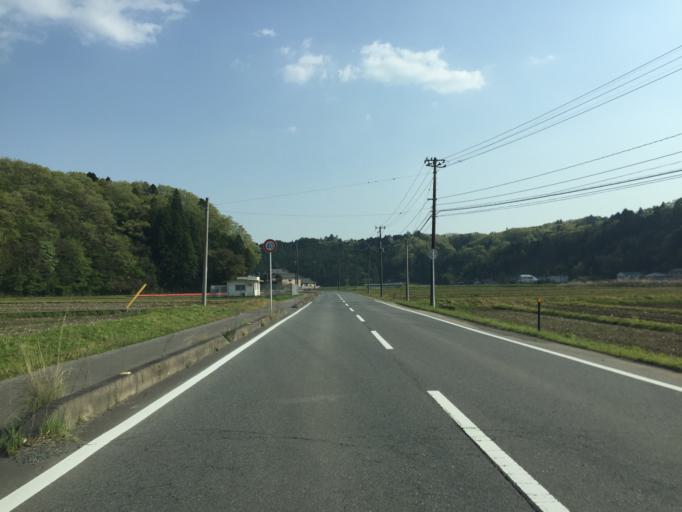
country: JP
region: Fukushima
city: Iwaki
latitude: 36.9739
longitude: 140.8019
